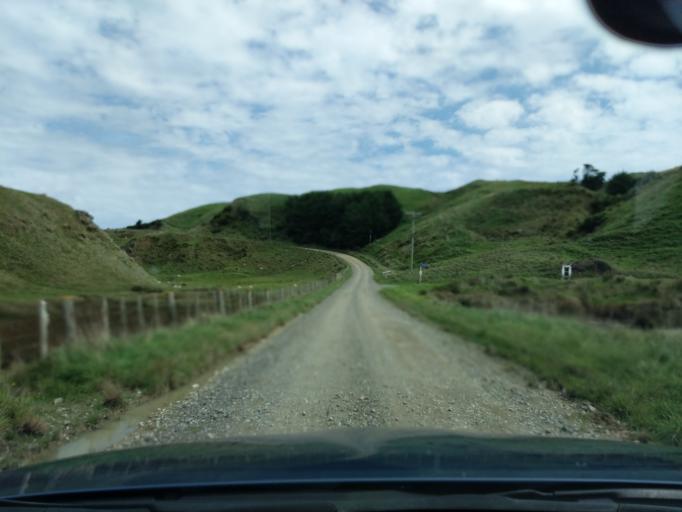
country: NZ
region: Tasman
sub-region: Tasman District
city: Takaka
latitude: -40.6459
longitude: 172.4320
